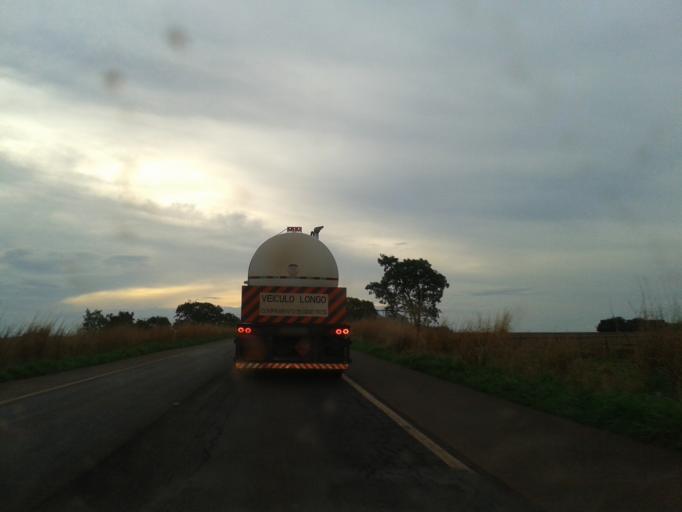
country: BR
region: Goias
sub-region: Santa Helena De Goias
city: Santa Helena de Goias
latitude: -17.9380
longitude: -50.5342
